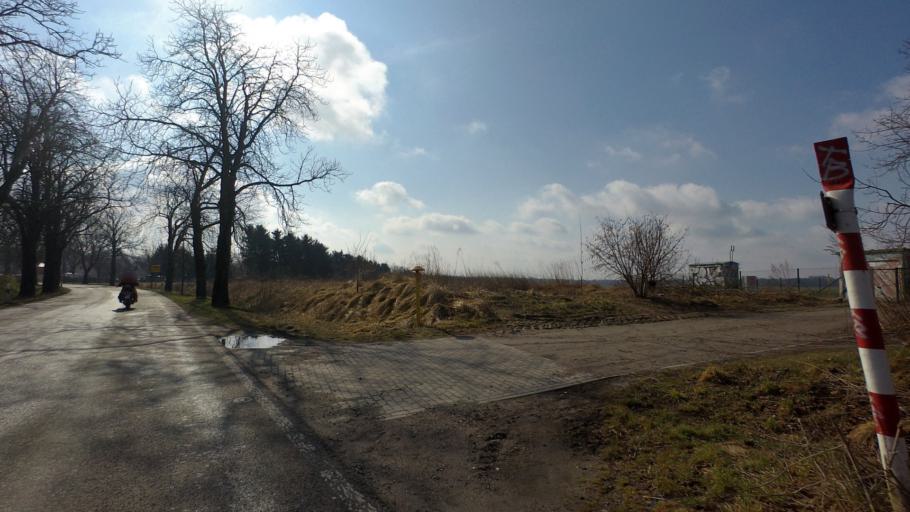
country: DE
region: Brandenburg
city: Glienicke
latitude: 52.6566
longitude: 13.3350
